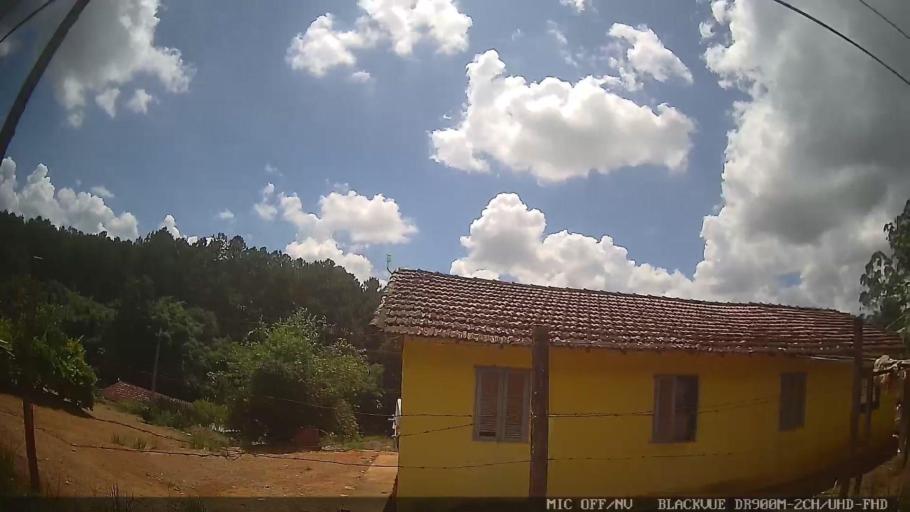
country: BR
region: Sao Paulo
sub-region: Jarinu
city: Jarinu
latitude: -23.1399
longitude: -46.6422
